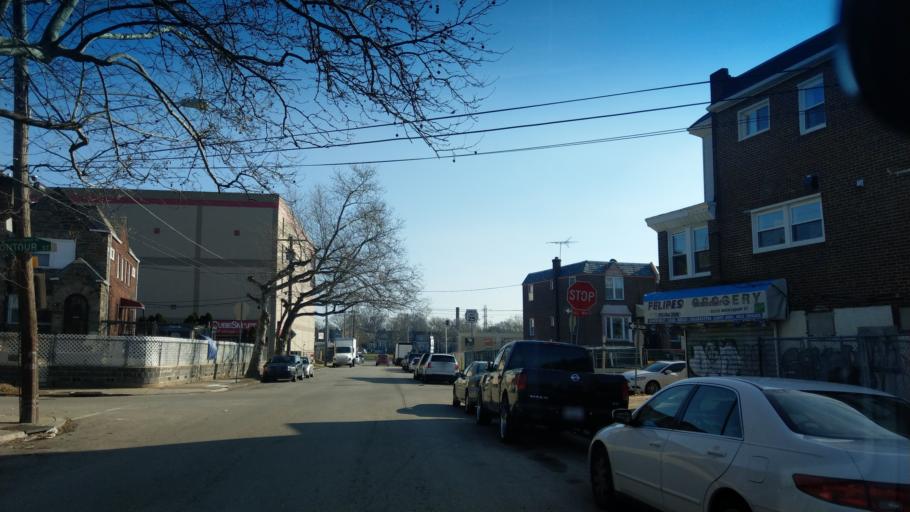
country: US
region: Pennsylvania
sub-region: Montgomery County
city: Rockledge
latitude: 40.0311
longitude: -75.1068
